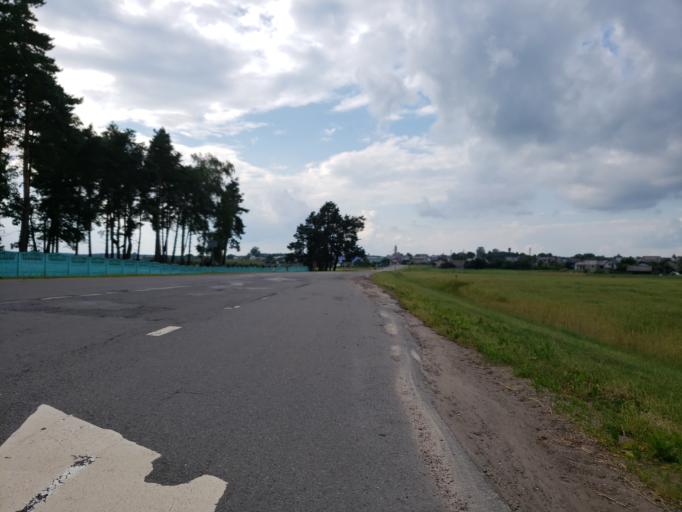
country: BY
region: Minsk
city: Chervyen'
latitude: 53.7266
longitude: 28.3913
